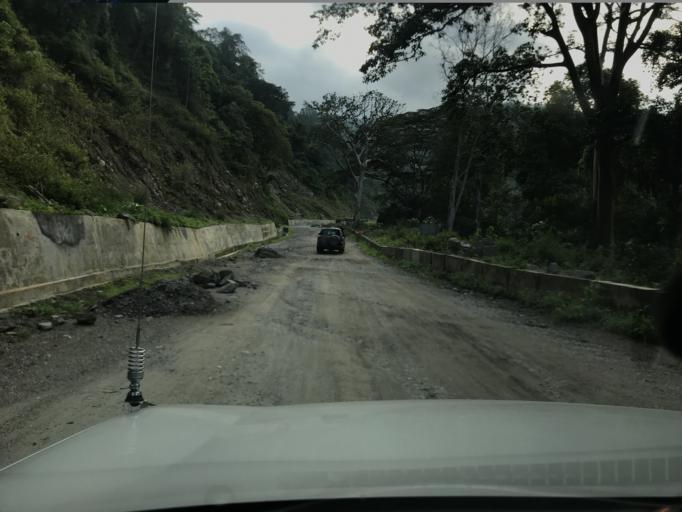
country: TL
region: Aileu
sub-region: Aileu Villa
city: Aileu
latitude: -8.6424
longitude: 125.5170
